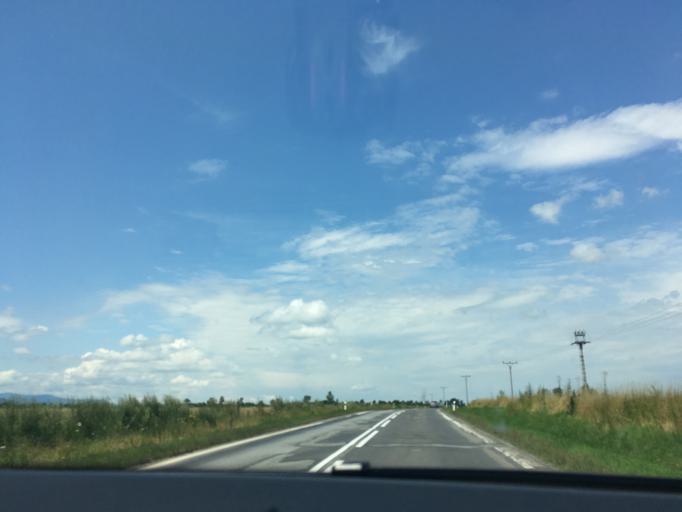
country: SK
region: Presovsky
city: Vranov nad Topl'ou
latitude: 48.8068
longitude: 21.6837
